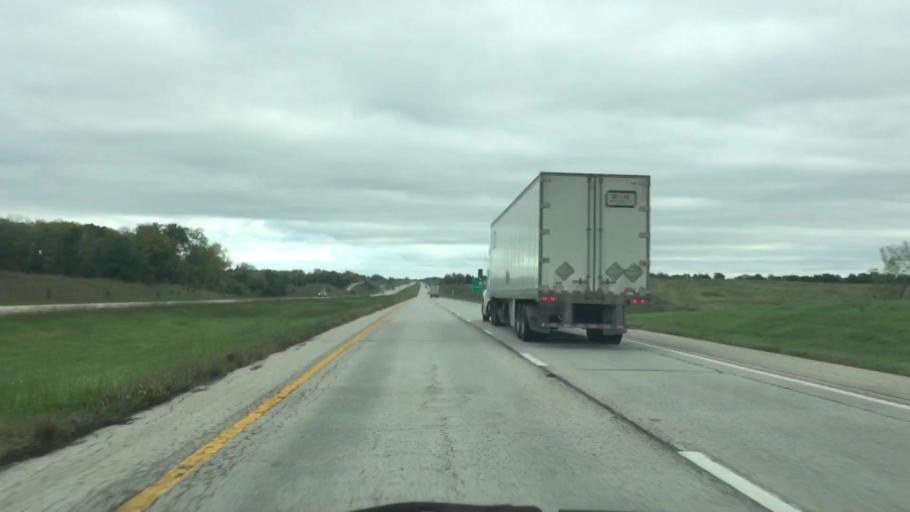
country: US
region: Missouri
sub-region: Harrison County
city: Bethany
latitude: 40.1380
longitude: -94.0454
